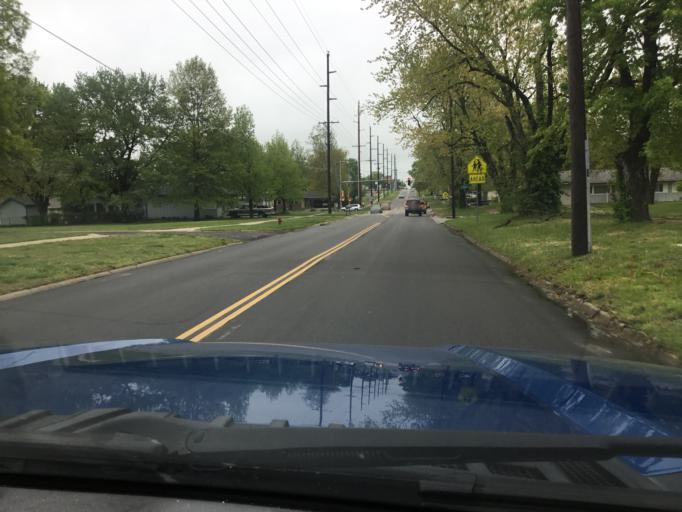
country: US
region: Kansas
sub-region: Shawnee County
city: Topeka
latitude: 39.0365
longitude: -95.7492
